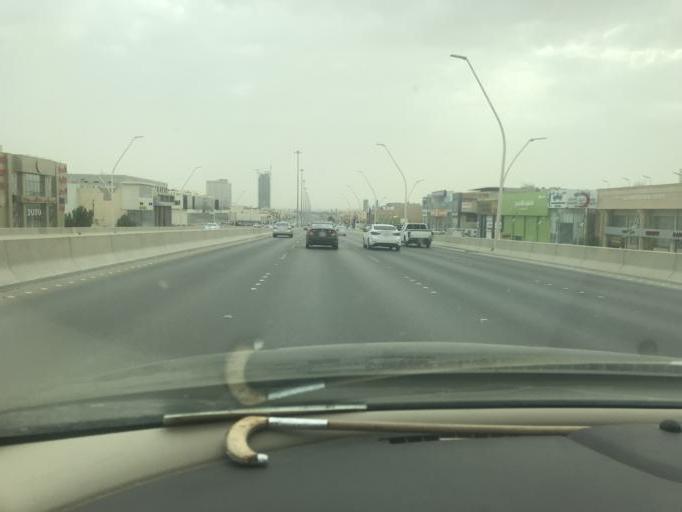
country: SA
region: Ar Riyad
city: Riyadh
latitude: 24.8182
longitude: 46.6417
